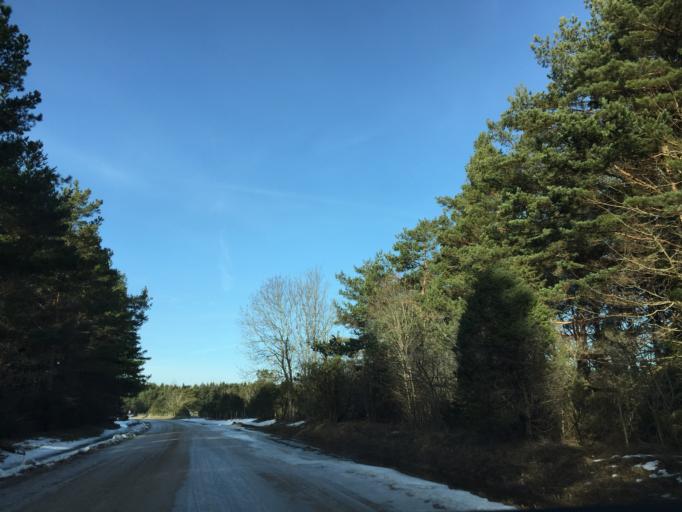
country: EE
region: Saare
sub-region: Kuressaare linn
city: Kuressaare
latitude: 58.3689
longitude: 22.0212
